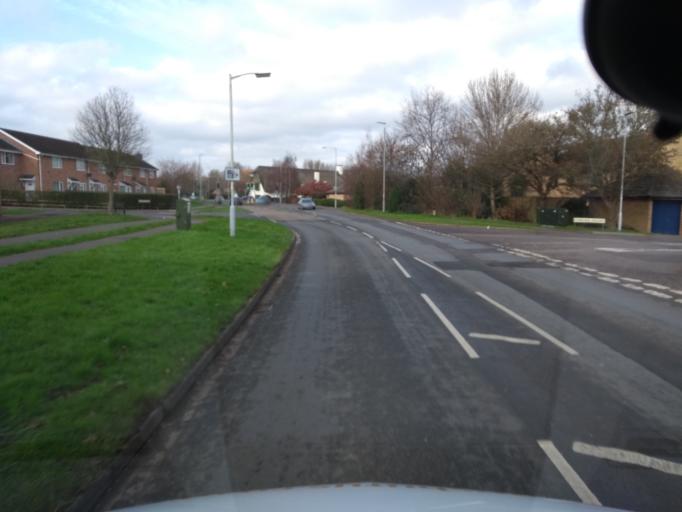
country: GB
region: England
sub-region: Somerset
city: Taunton
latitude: 51.0125
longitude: -3.0764
